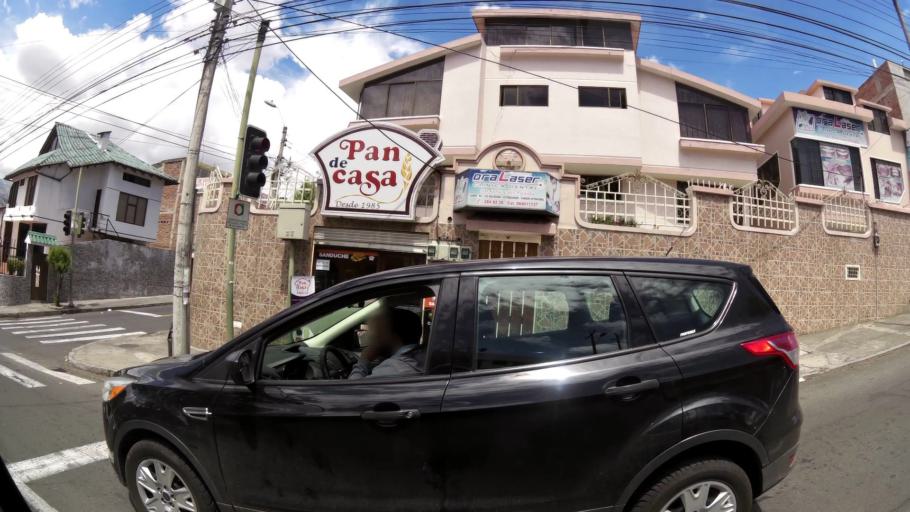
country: EC
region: Tungurahua
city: Ambato
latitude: -1.2592
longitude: -78.6401
